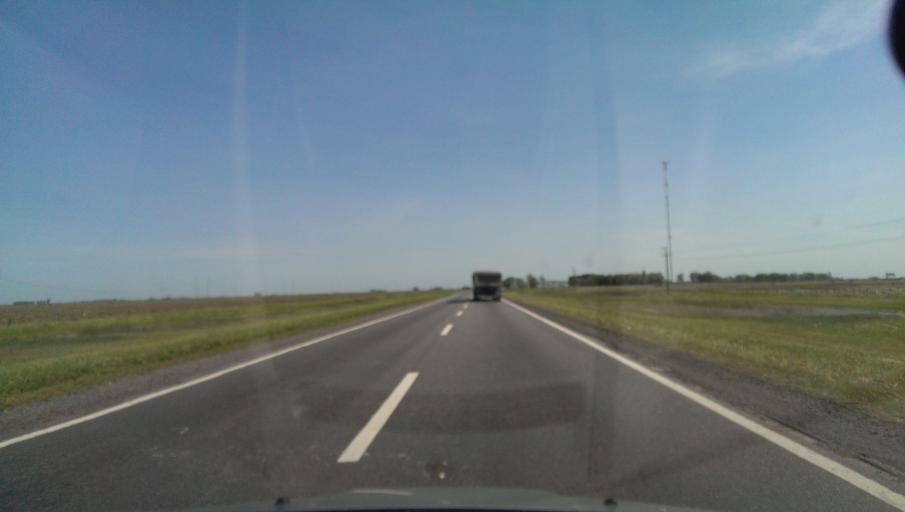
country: AR
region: Buenos Aires
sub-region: Partido de Azul
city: Azul
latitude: -36.6042
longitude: -59.6699
